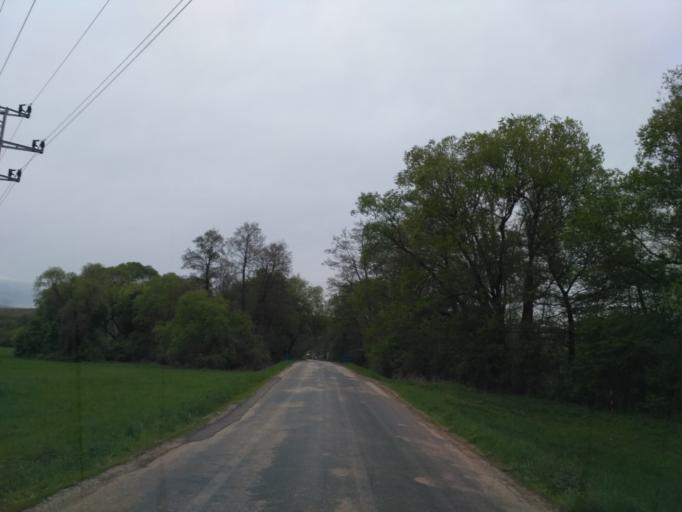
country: SK
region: Kosicky
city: Moldava nad Bodvou
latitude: 48.6474
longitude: 21.0025
